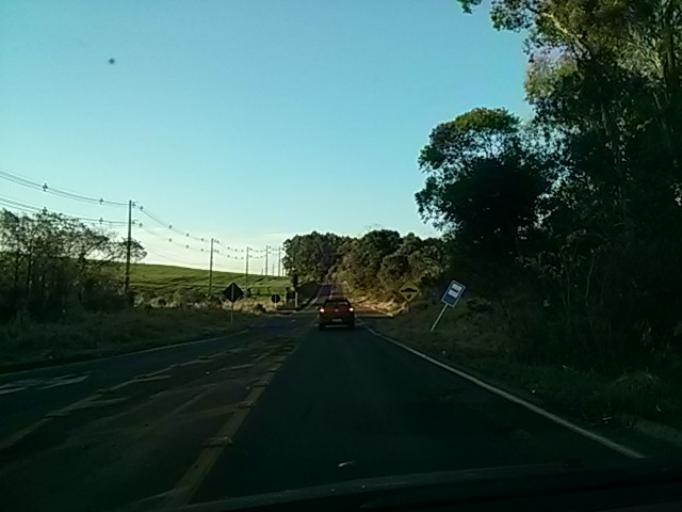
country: BR
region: Santa Catarina
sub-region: Chapeco
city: Chapeco
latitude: -27.1095
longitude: -52.7100
